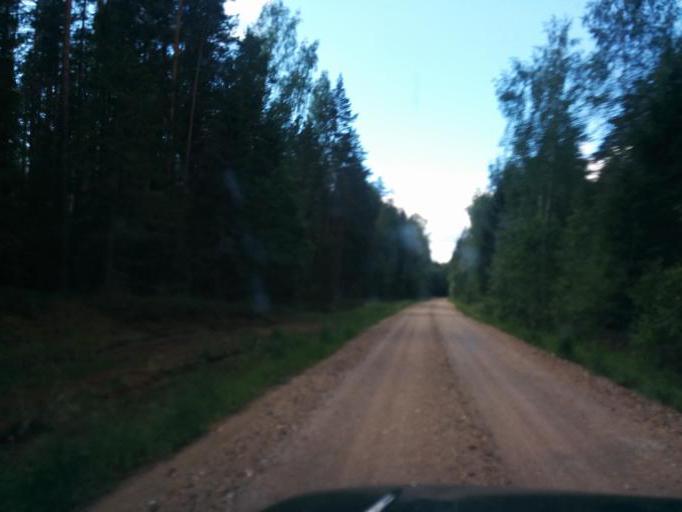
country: LV
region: Vilaka
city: Vilaka
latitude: 57.3254
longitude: 27.6730
